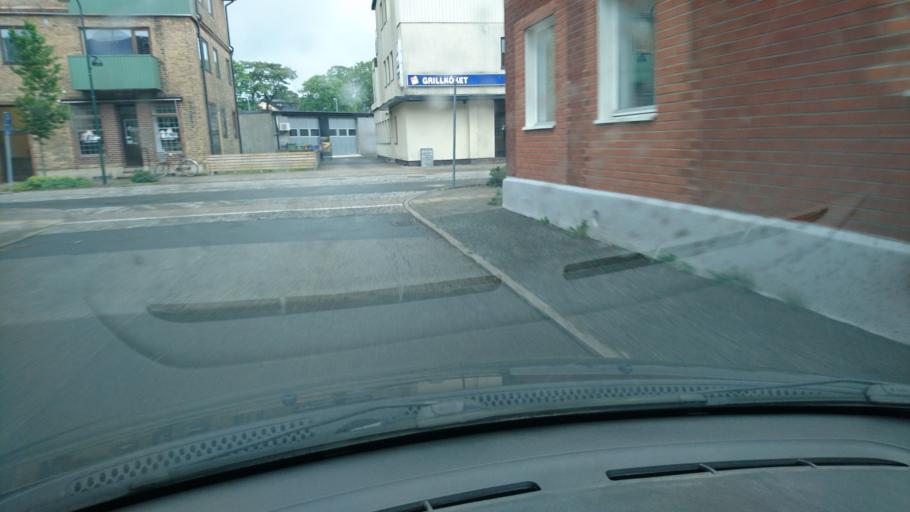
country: SE
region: Skane
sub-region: Tomelilla Kommun
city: Tomelilla
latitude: 55.5453
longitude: 13.9512
